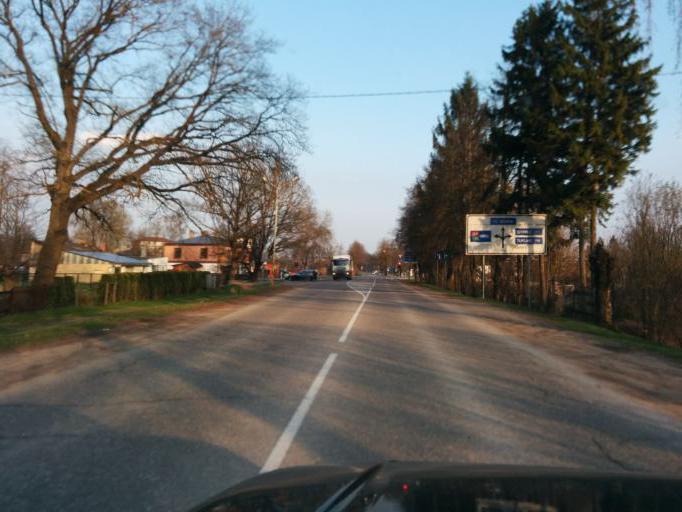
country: LV
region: Jelgava
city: Jelgava
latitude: 56.6586
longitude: 23.7407
